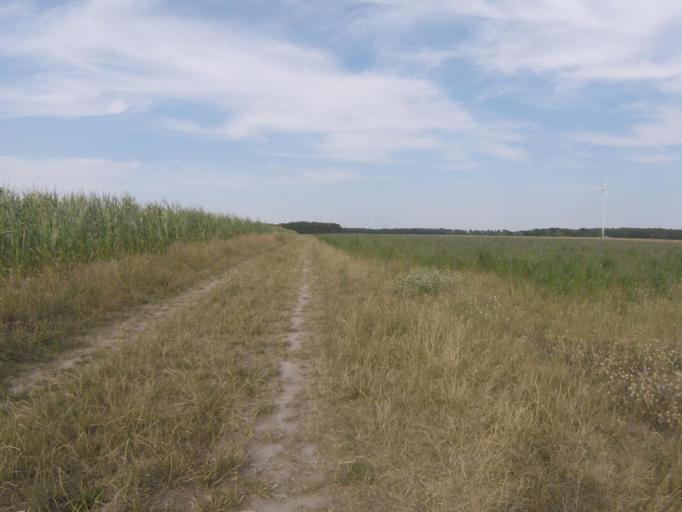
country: DE
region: Brandenburg
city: Konigs Wusterhausen
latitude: 52.3056
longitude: 13.7269
